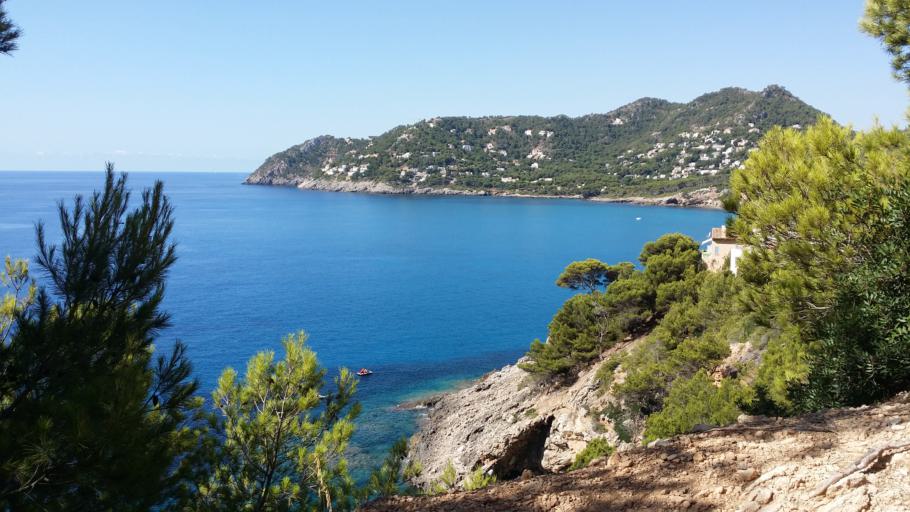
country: ES
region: Balearic Islands
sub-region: Illes Balears
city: Capdepera
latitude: 39.6566
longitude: 3.4490
